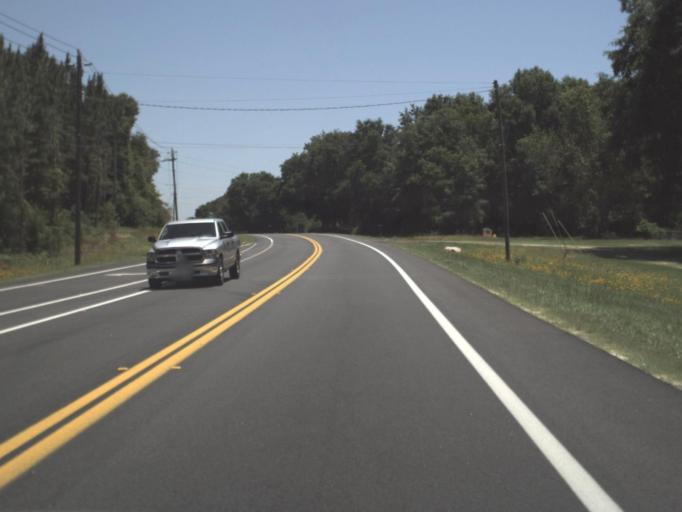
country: US
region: Florida
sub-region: Suwannee County
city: Wellborn
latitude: 30.1955
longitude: -82.7579
